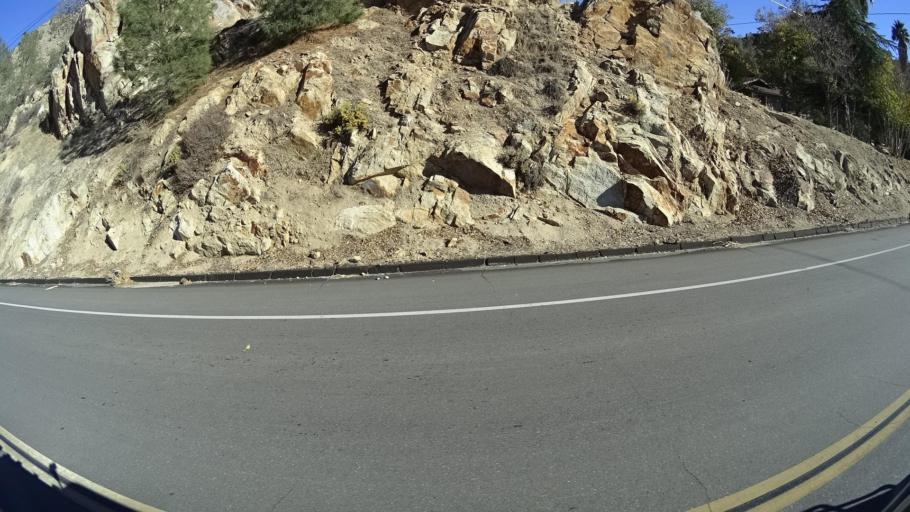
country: US
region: California
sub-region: Kern County
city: Kernville
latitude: 35.7408
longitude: -118.4146
